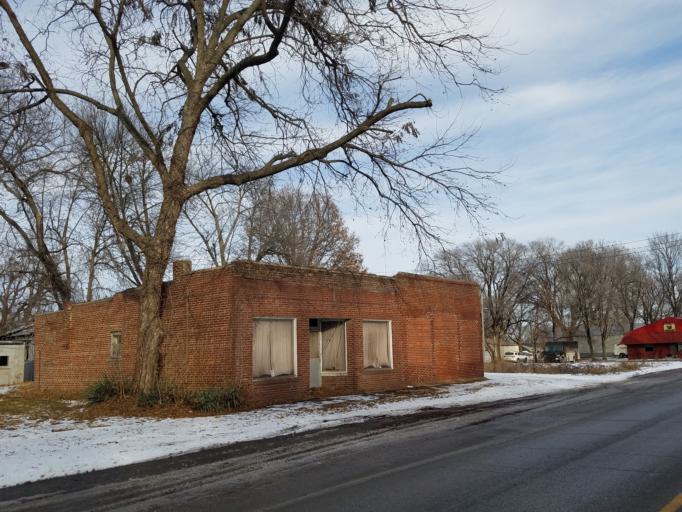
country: US
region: Missouri
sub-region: Saline County
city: Marshall
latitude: 39.1938
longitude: -93.3641
